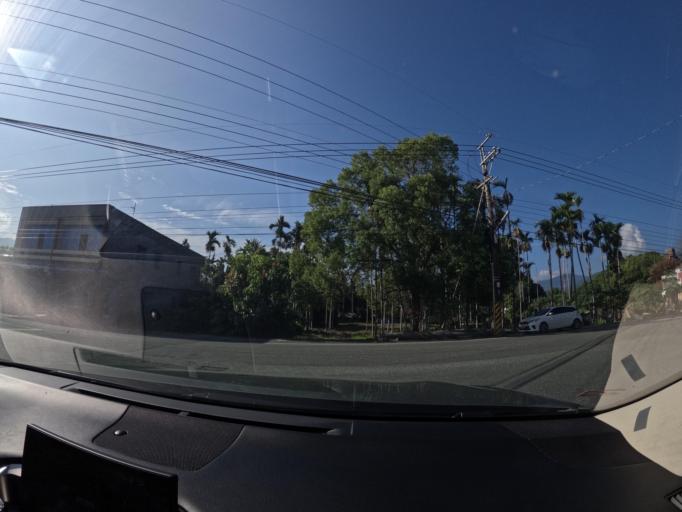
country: TW
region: Taiwan
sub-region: Hualien
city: Hualian
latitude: 23.4941
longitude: 121.3793
